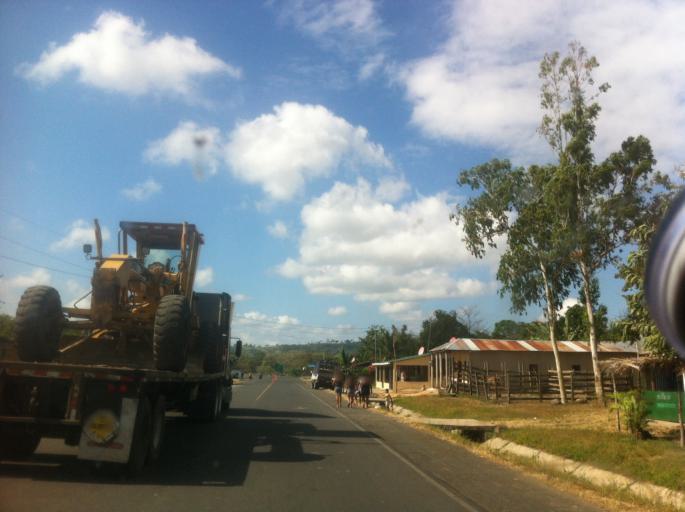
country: NI
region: Rio San Juan
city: San Carlos
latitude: 11.2282
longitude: -84.6920
